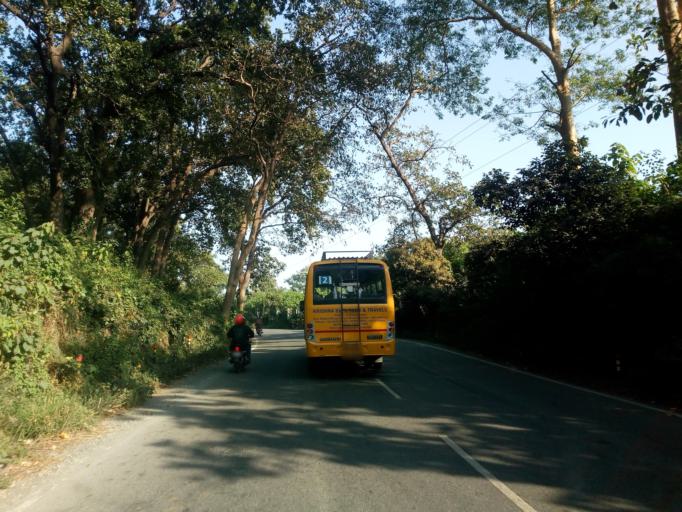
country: IN
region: Uttarakhand
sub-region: Dehradun
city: Vikasnagar
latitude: 30.3469
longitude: 77.8750
